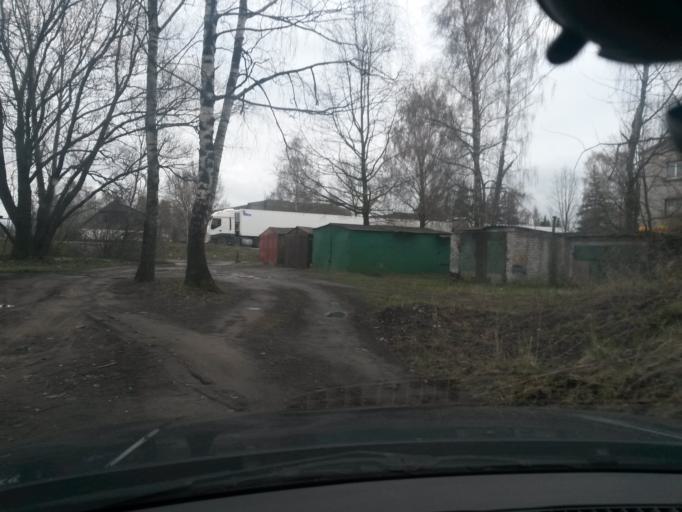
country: LV
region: Kekava
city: Kekava
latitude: 56.8965
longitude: 24.2262
